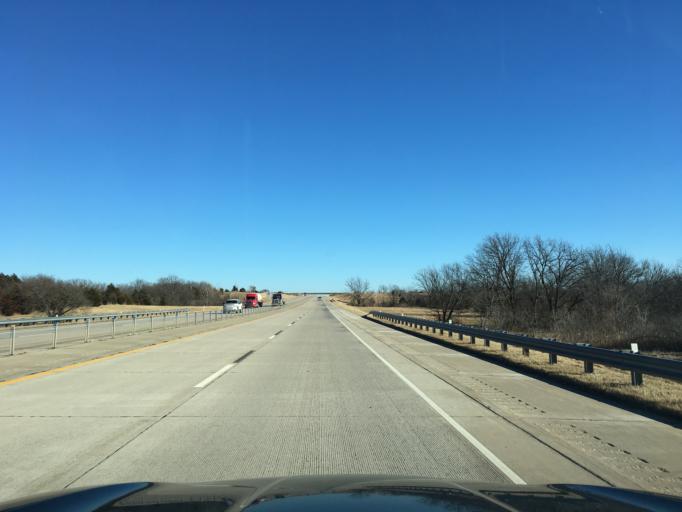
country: US
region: Oklahoma
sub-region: Payne County
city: Yale
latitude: 36.2249
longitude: -96.7060
